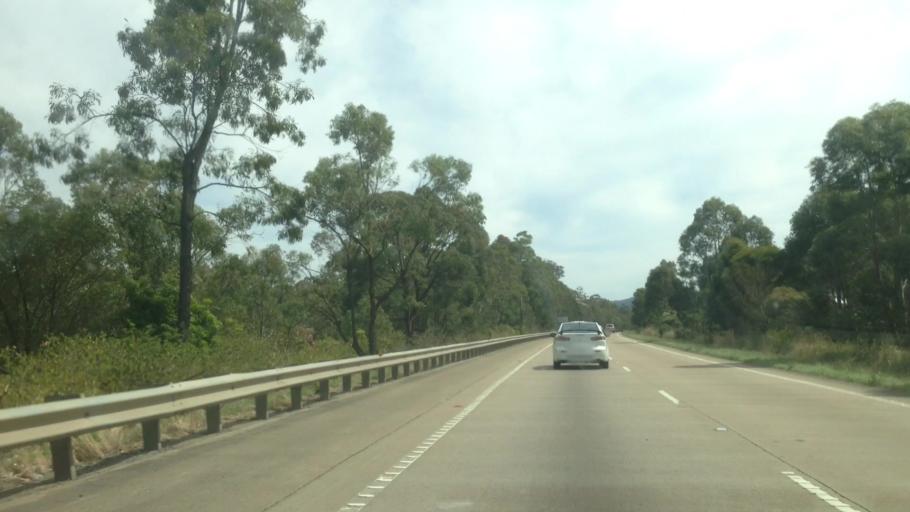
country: AU
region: New South Wales
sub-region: Lake Macquarie Shire
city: Holmesville
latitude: -32.8940
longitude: 151.5936
